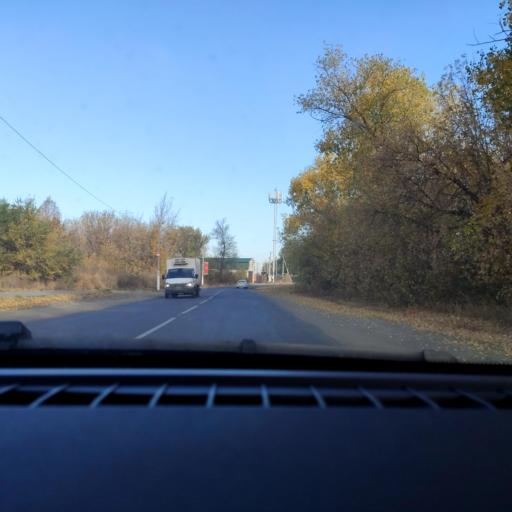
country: RU
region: Voronezj
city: Somovo
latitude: 51.6744
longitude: 39.3220
